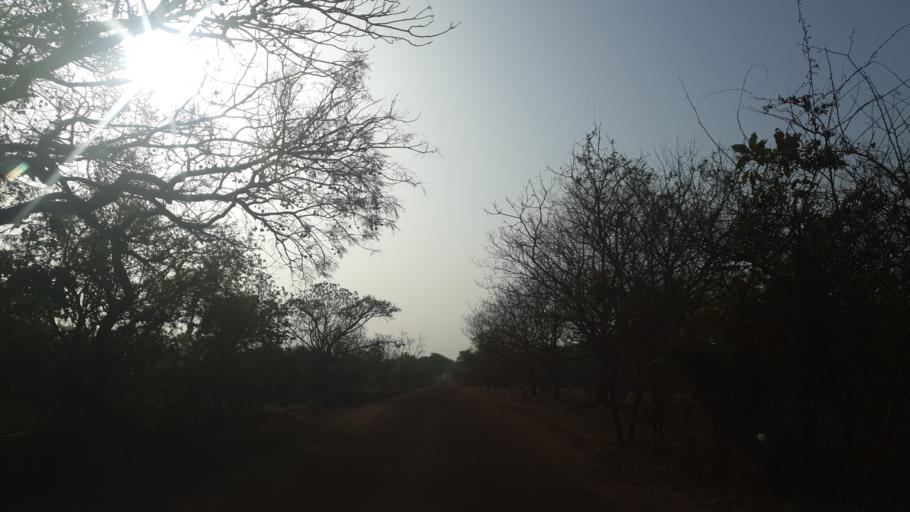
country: ML
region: Sikasso
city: Kolondieba
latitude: 10.8970
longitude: -6.8867
